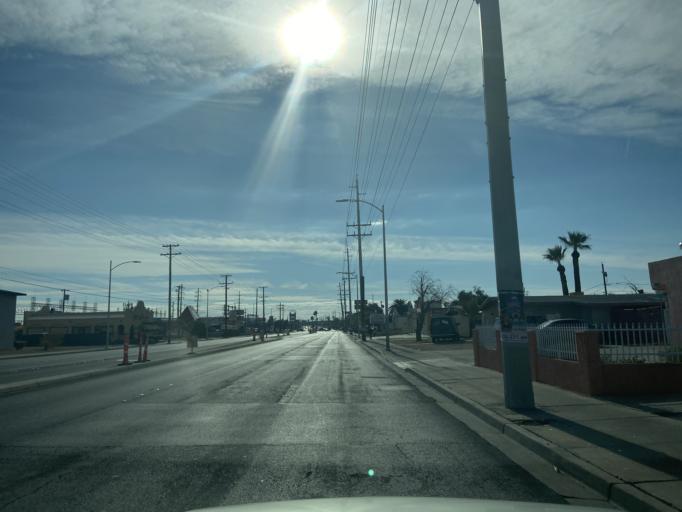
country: US
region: Nevada
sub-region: Clark County
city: Las Vegas
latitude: 36.1769
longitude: -115.1162
